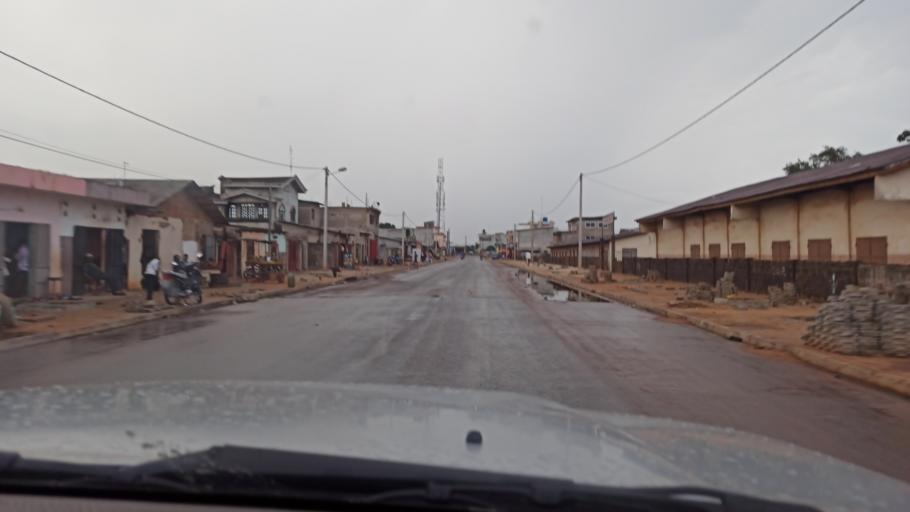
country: BJ
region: Queme
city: Porto-Novo
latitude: 6.4958
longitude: 2.6415
